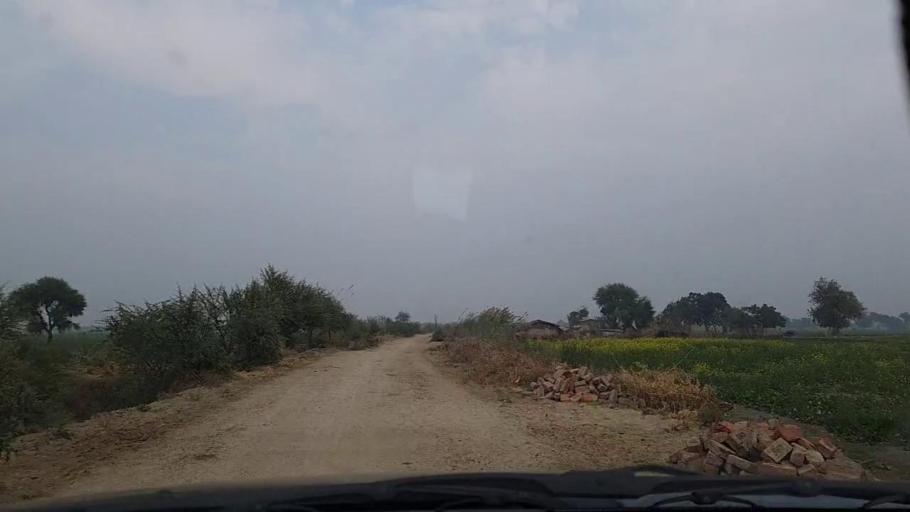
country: PK
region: Sindh
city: Tando Mittha Khan
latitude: 25.8080
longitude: 69.3786
